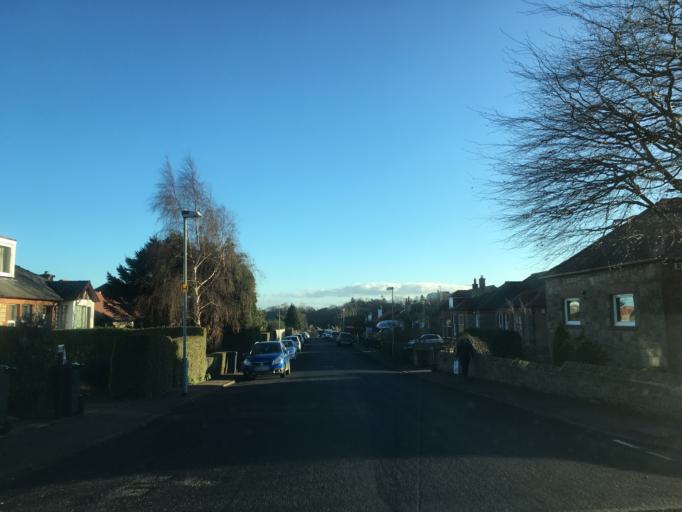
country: GB
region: Scotland
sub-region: Edinburgh
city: Colinton
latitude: 55.9594
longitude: -3.2574
